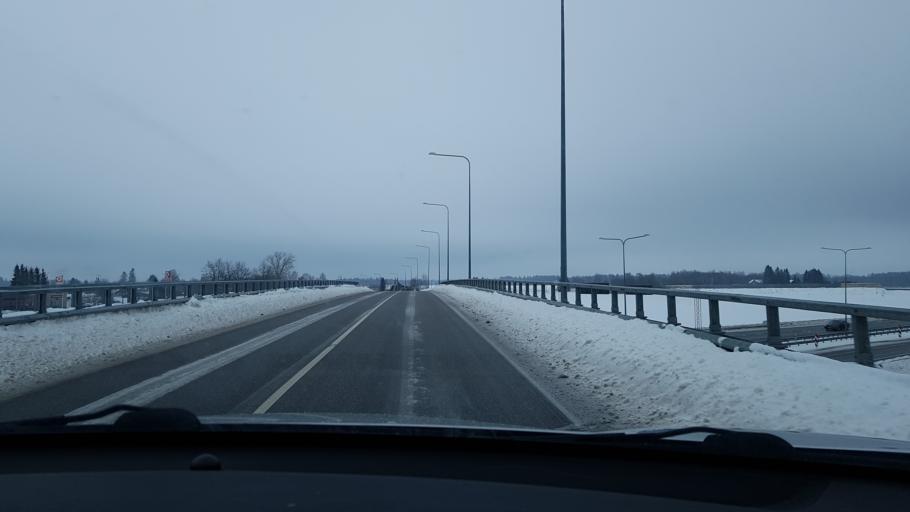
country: EE
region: Jaervamaa
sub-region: Paide linn
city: Paide
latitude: 58.9162
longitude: 25.6113
